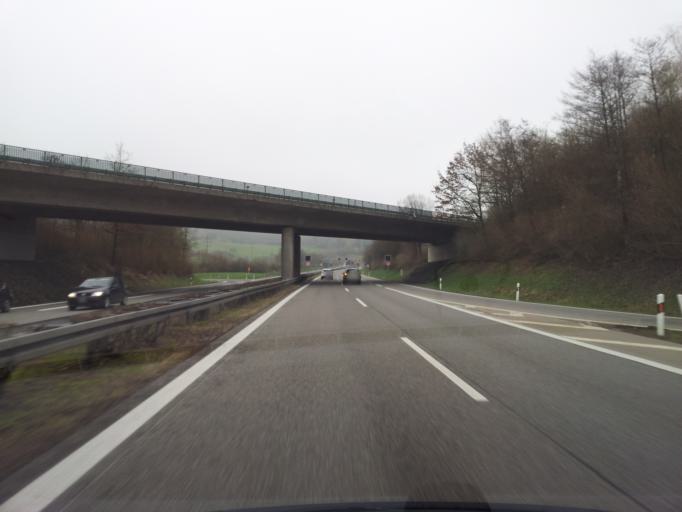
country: DE
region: Baden-Wuerttemberg
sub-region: Freiburg Region
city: Hilzingen
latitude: 47.7619
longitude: 8.7968
